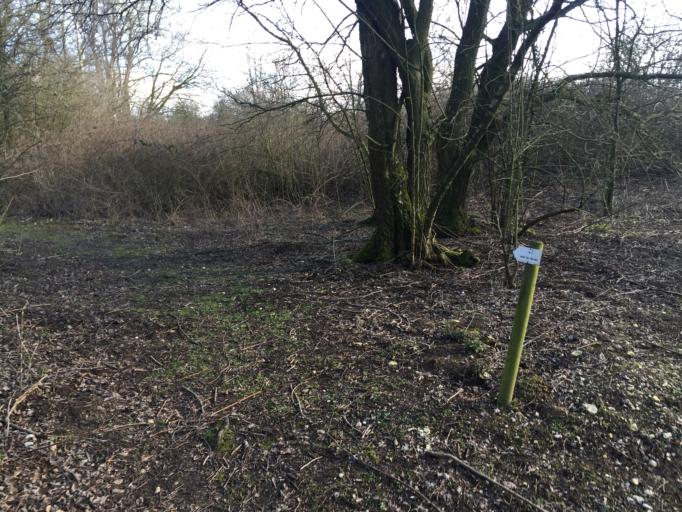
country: BE
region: Flanders
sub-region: Provincie Limburg
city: Sint-Pieters-Voeren
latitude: 50.7222
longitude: 5.7903
